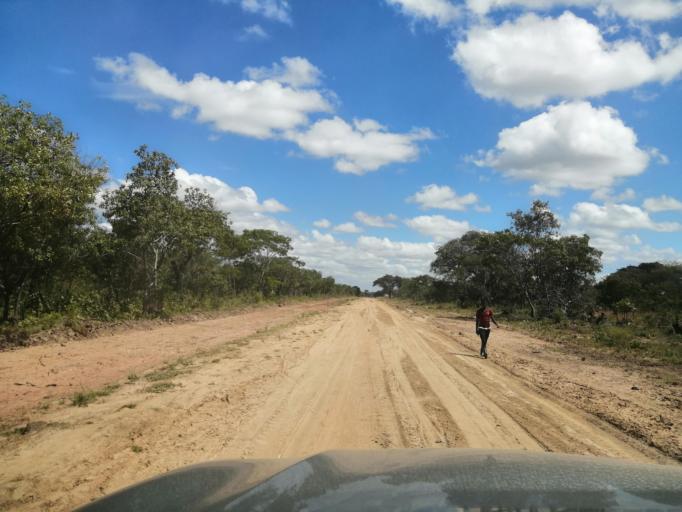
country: ZM
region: Central
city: Mumbwa
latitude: -14.5781
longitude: 27.2472
